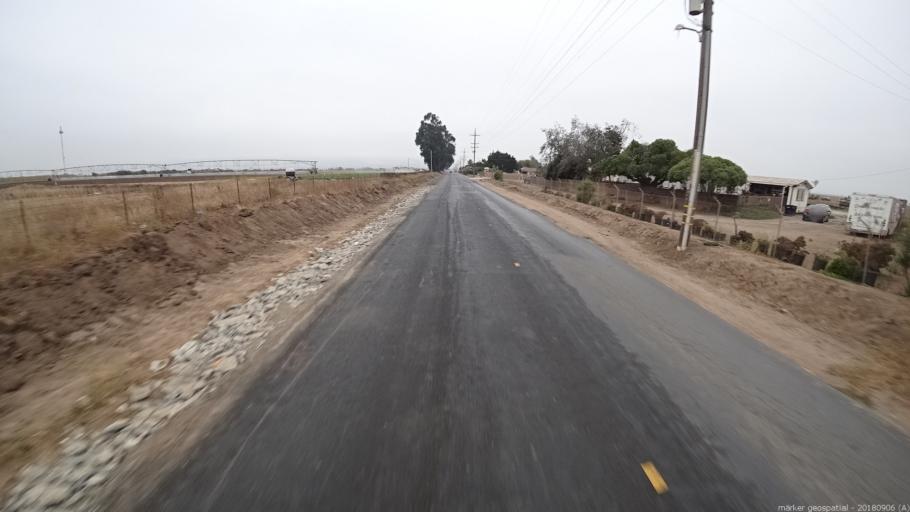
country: US
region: California
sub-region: Monterey County
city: Chualar
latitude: 36.6253
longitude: -121.5473
